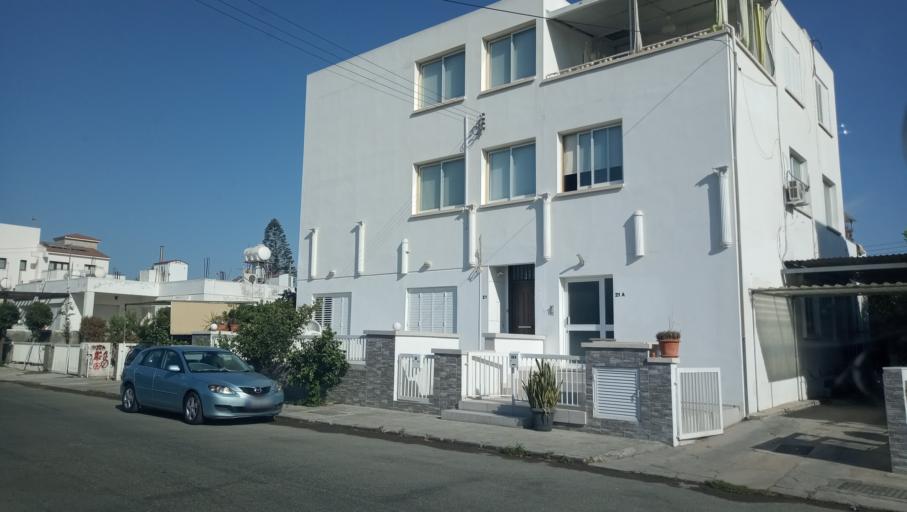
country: CY
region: Lefkosia
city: Nicosia
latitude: 35.1479
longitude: 33.3876
